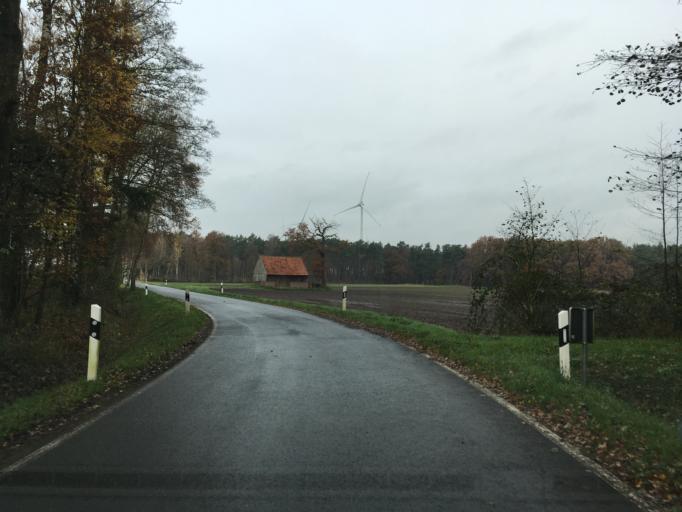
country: DE
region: North Rhine-Westphalia
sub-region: Regierungsbezirk Munster
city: Ahaus
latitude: 52.0192
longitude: 6.9965
